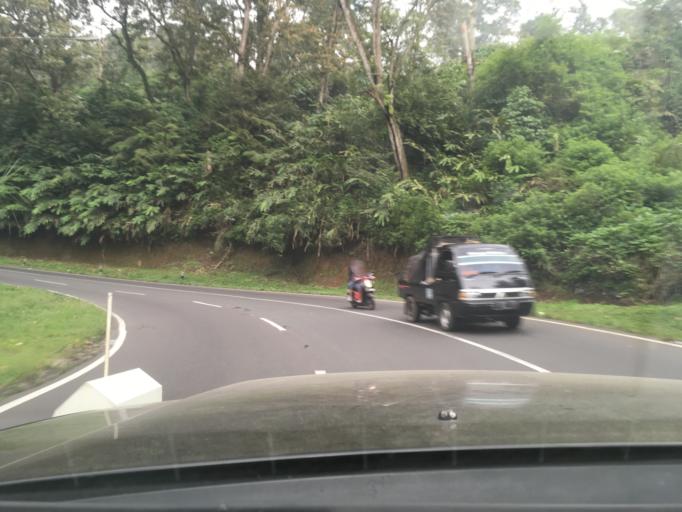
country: ID
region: West Java
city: Lembang
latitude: -6.7697
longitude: 107.6359
